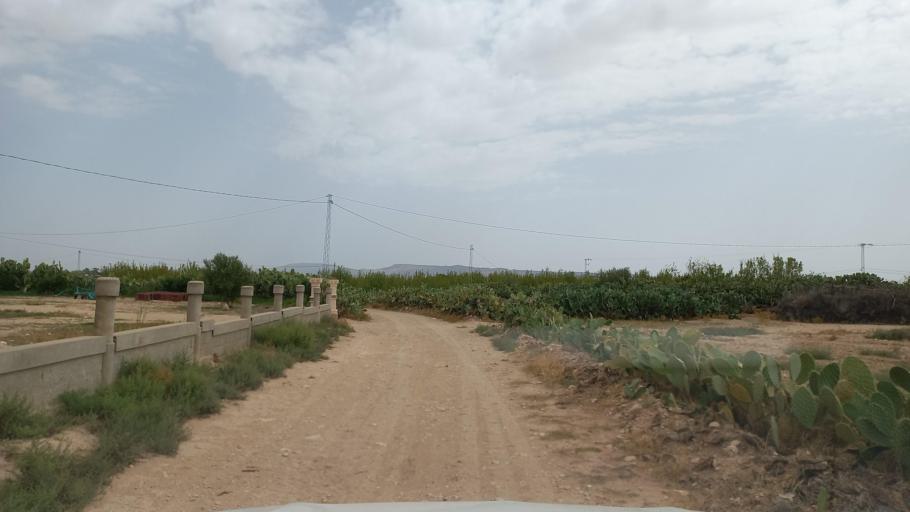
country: TN
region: Al Qasrayn
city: Kasserine
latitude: 35.2831
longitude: 9.0212
